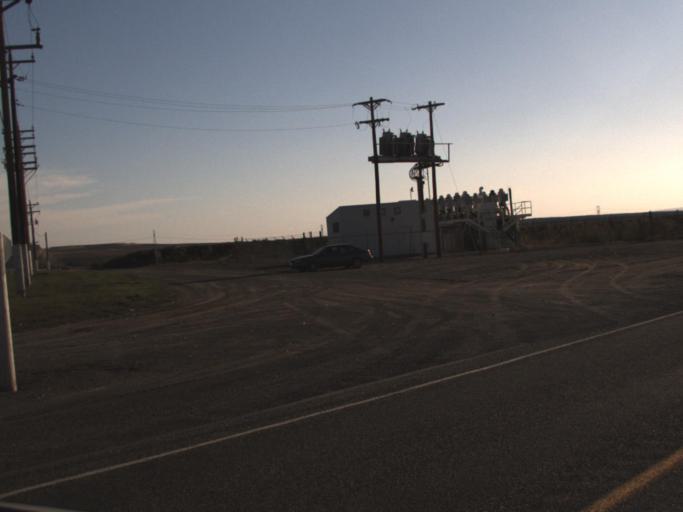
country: US
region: Washington
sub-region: Walla Walla County
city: Burbank
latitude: 46.2309
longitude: -118.8469
